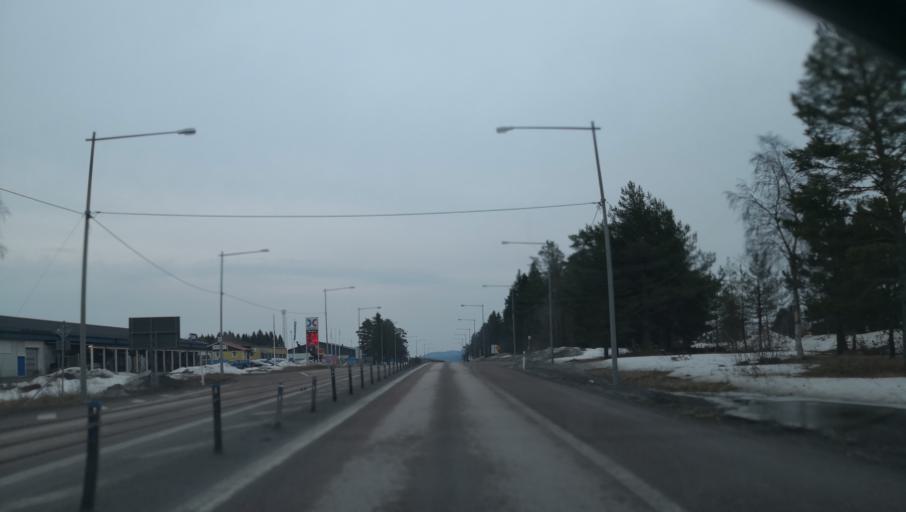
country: SE
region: Vaesternorrland
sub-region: Haernoesands Kommun
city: Haernoesand
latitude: 62.6499
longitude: 17.8931
